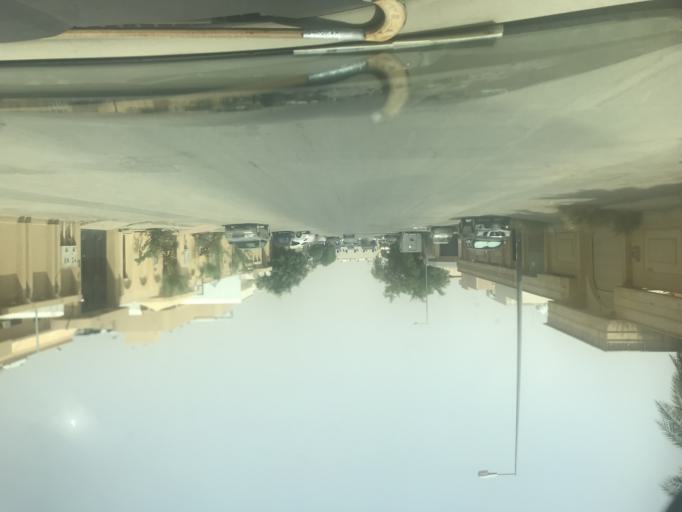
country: SA
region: Ar Riyad
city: Riyadh
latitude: 24.7446
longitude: 46.7871
